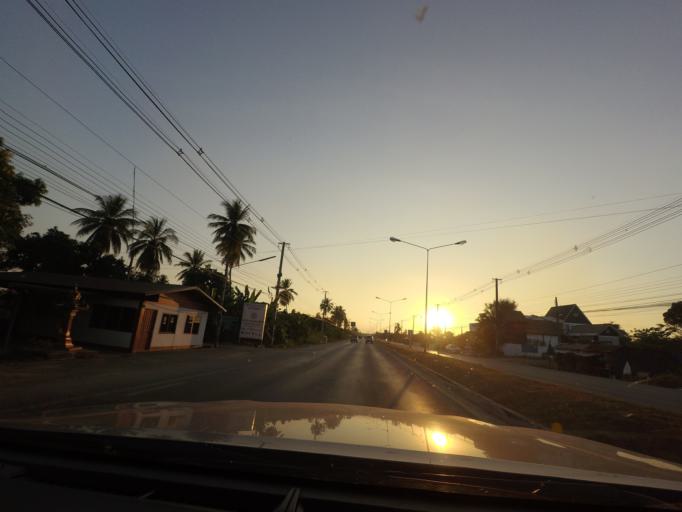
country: TH
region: Sukhothai
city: Sukhothai
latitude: 17.0536
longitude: 99.8293
